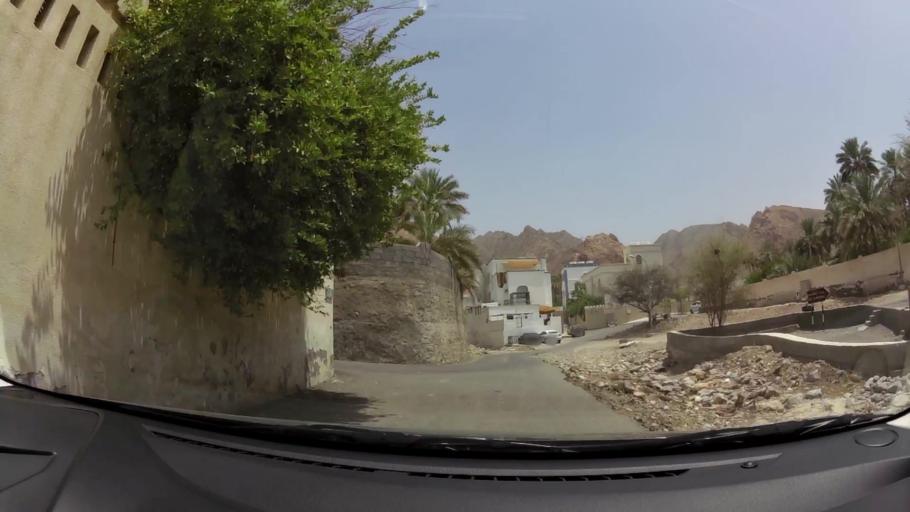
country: OM
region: Muhafazat Masqat
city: Bawshar
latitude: 23.5342
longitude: 58.3915
